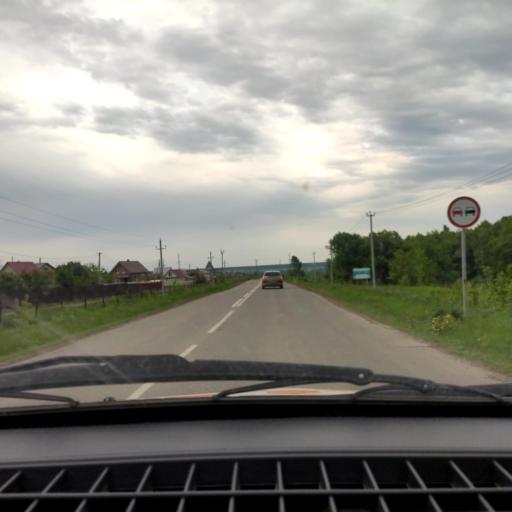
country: RU
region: Bashkortostan
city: Avdon
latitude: 54.5770
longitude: 55.7527
